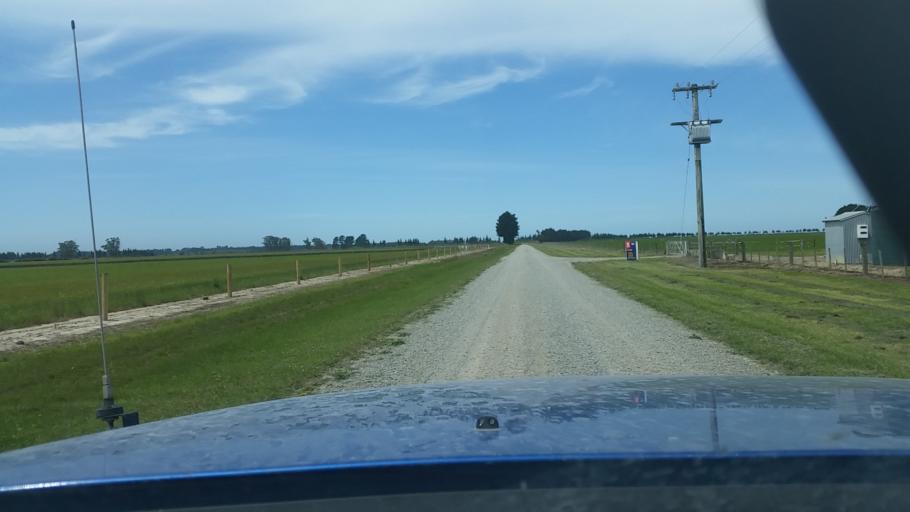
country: NZ
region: Canterbury
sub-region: Ashburton District
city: Tinwald
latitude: -44.0554
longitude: 171.7784
